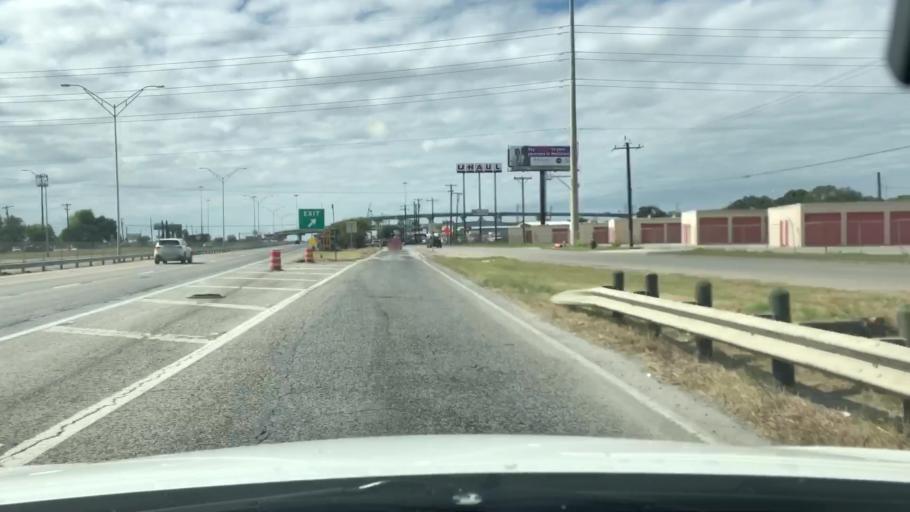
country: US
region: Texas
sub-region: Bexar County
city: Lackland Air Force Base
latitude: 29.3994
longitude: -98.6423
